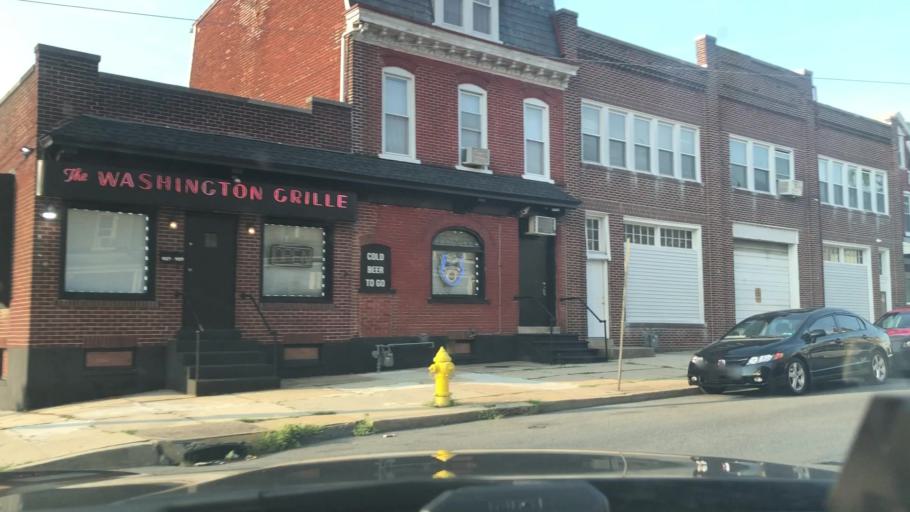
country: US
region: Pennsylvania
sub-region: Lehigh County
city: Allentown
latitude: 40.6119
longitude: -75.4820
